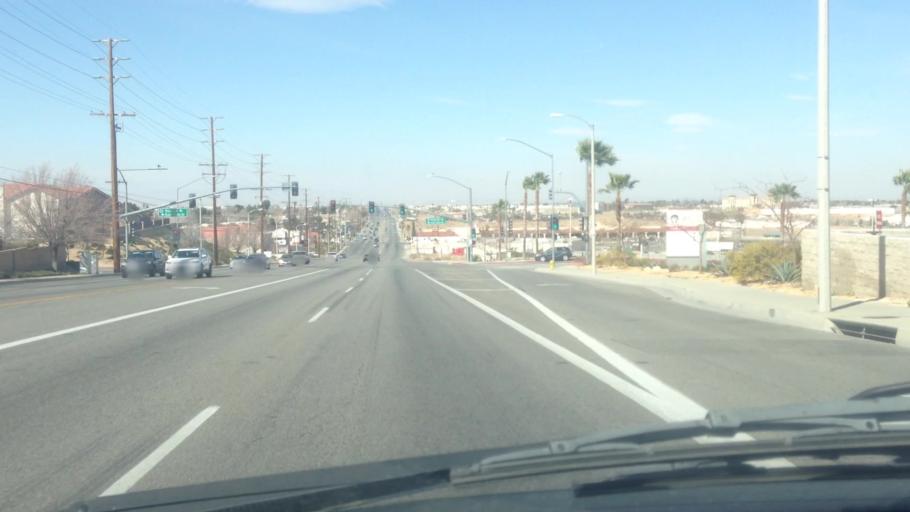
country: US
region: California
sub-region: Los Angeles County
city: Desert View Highlands
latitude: 34.5829
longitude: -118.1474
